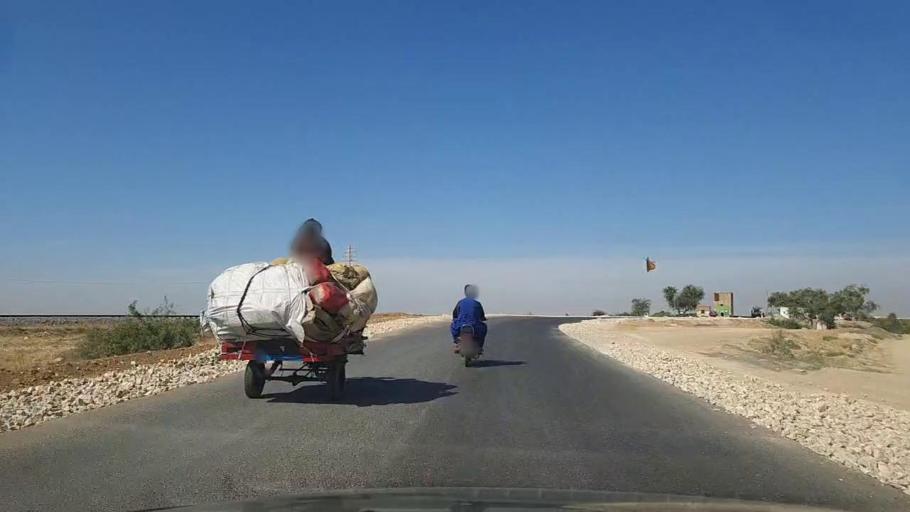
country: PK
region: Sindh
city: Kotri
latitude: 25.2947
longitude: 68.2040
